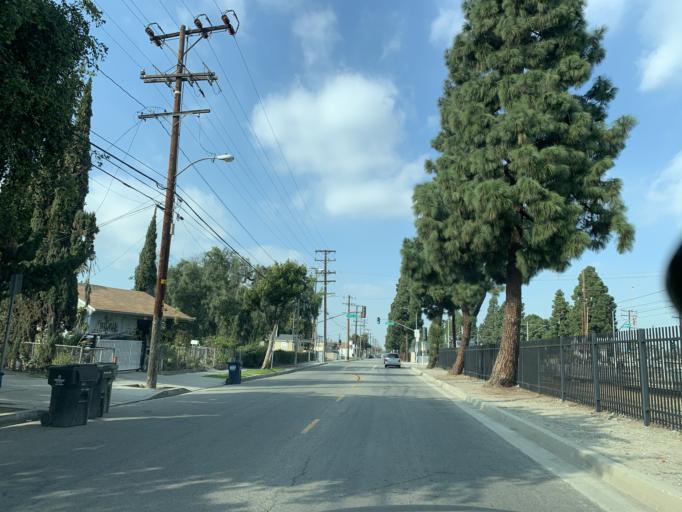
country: US
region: California
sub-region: Los Angeles County
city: Willowbrook
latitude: 33.9192
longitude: -118.2333
